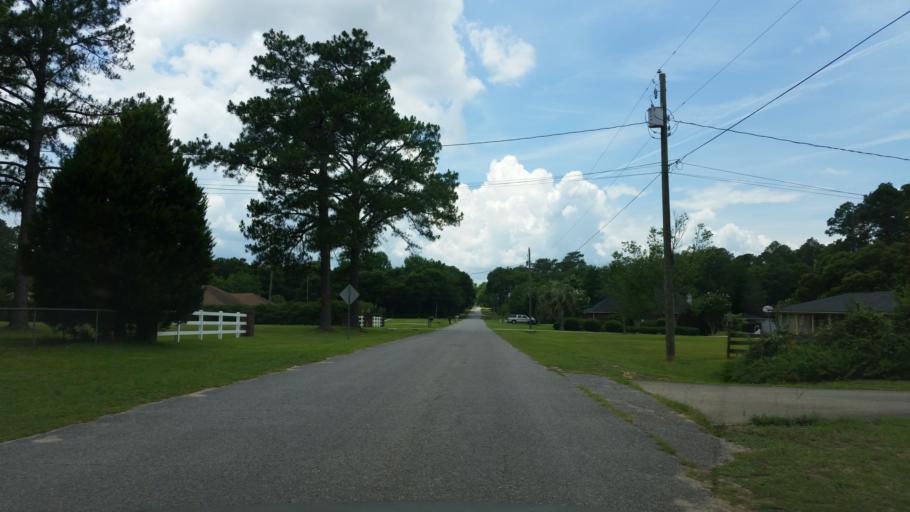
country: US
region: Florida
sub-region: Escambia County
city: Gonzalez
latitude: 30.5466
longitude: -87.3048
